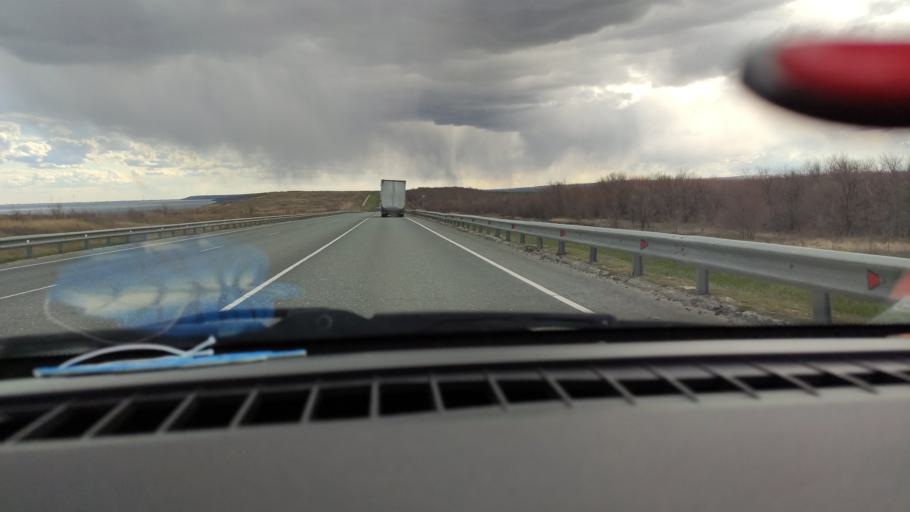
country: RU
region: Saratov
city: Alekseyevka
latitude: 52.2126
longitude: 47.8838
